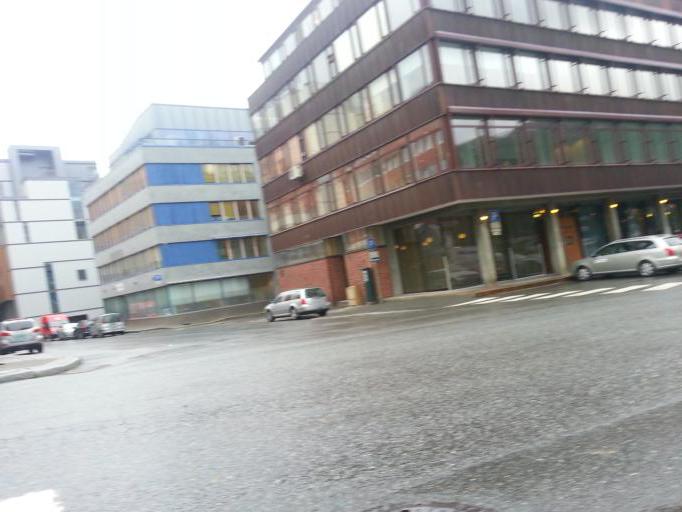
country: NO
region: Troms
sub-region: Tromso
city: Tromso
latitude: 69.6481
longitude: 18.9597
